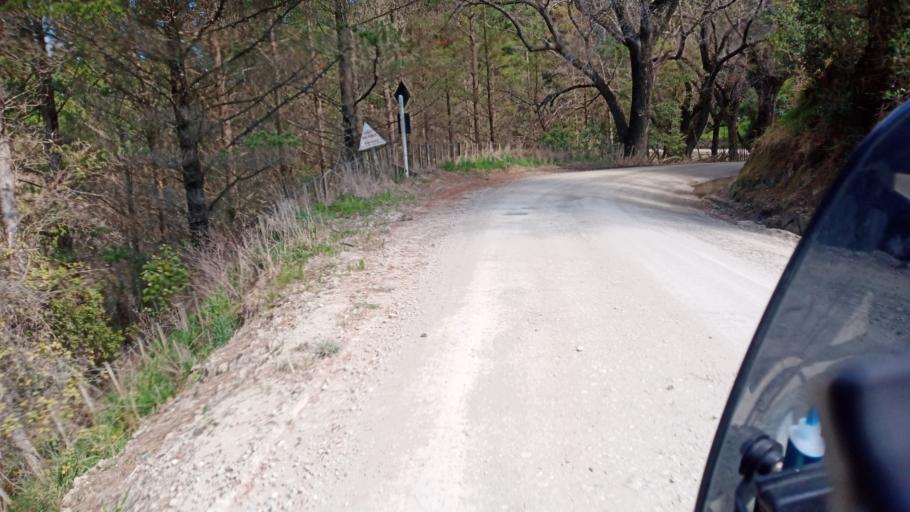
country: NZ
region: Gisborne
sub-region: Gisborne District
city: Gisborne
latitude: -38.8120
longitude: 177.7656
